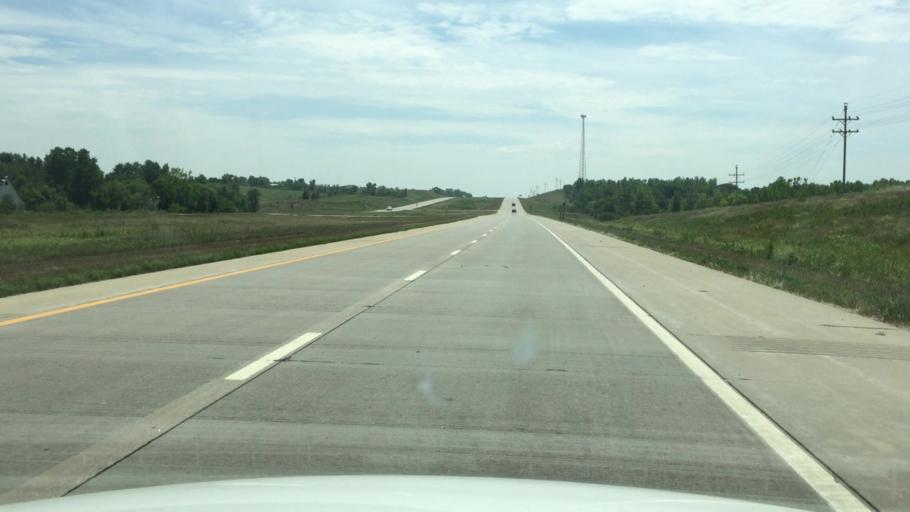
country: US
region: Kansas
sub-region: Shawnee County
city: Silver Lake
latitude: 39.2565
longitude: -95.7201
